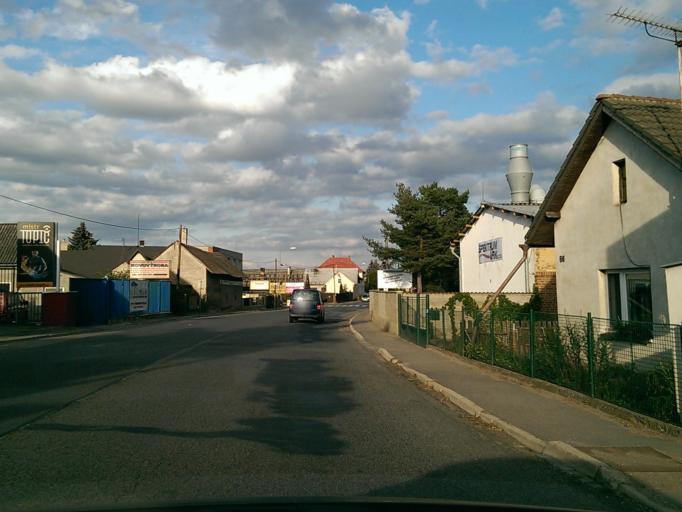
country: CZ
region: Central Bohemia
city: Knezmost
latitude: 50.4254
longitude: 15.0267
